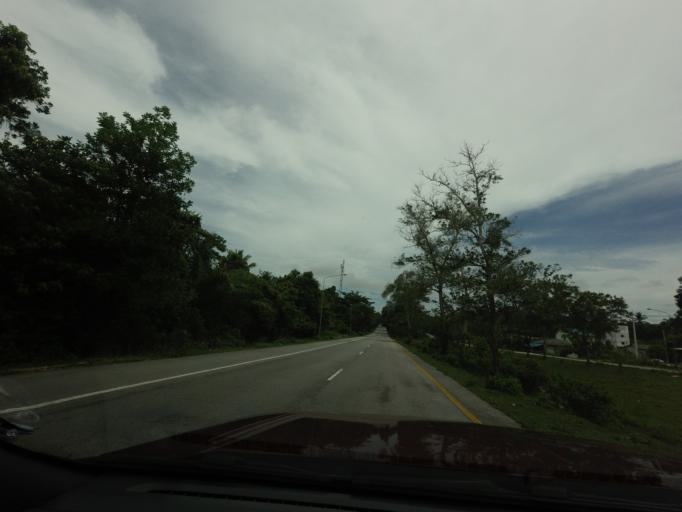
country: TH
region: Narathiwat
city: Narathiwat
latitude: 6.3457
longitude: 101.8573
